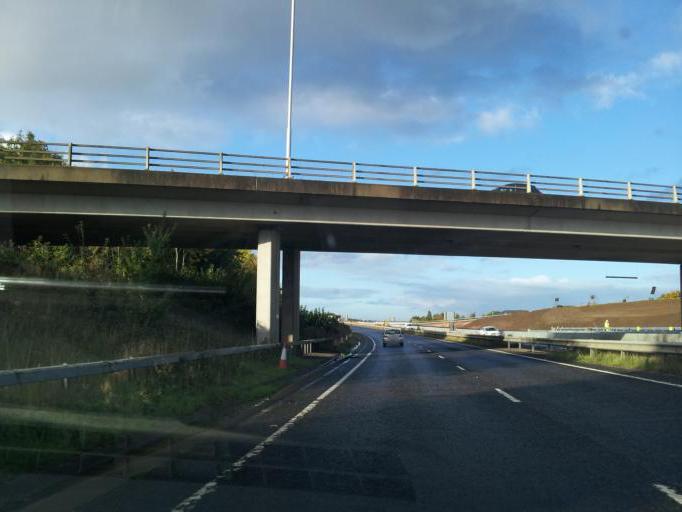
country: GB
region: England
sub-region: Norfolk
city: Surlingham
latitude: 52.6261
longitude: 1.3798
